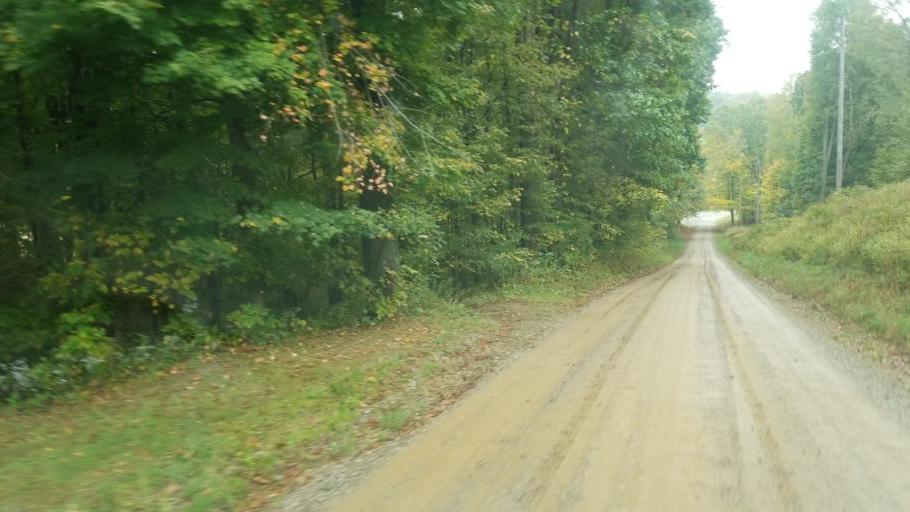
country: US
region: Ohio
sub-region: Knox County
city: Danville
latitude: 40.4963
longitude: -82.3485
